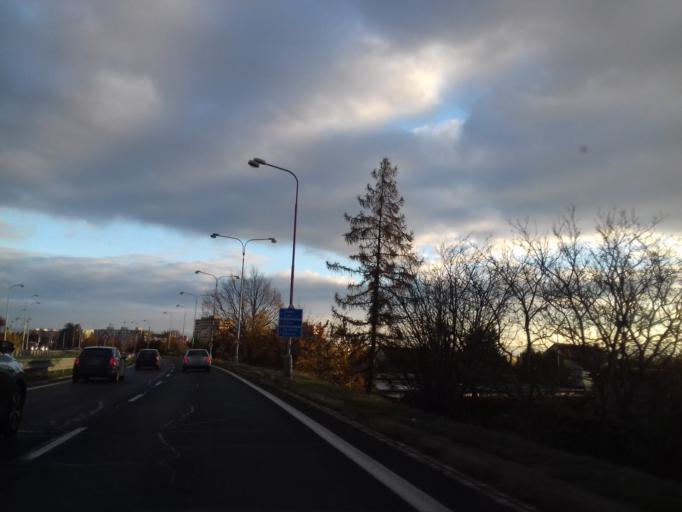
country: CZ
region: Olomoucky
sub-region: Okres Olomouc
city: Olomouc
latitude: 49.5741
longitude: 17.2353
